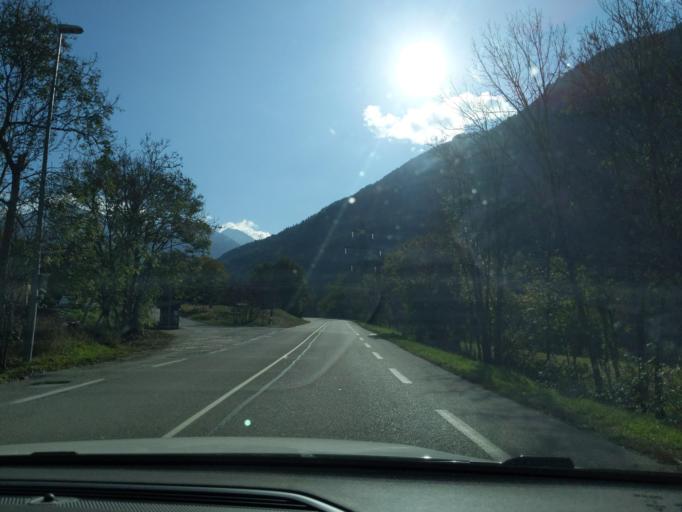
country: FR
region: Rhone-Alpes
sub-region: Departement de la Savoie
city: Seez
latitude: 45.6145
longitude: 6.8228
